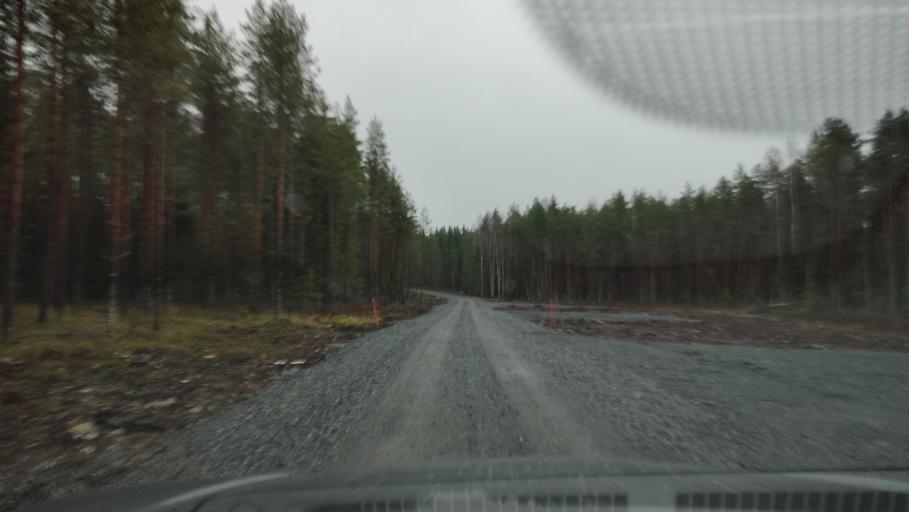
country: FI
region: Southern Ostrobothnia
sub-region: Suupohja
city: Karijoki
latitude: 62.1545
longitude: 21.6071
